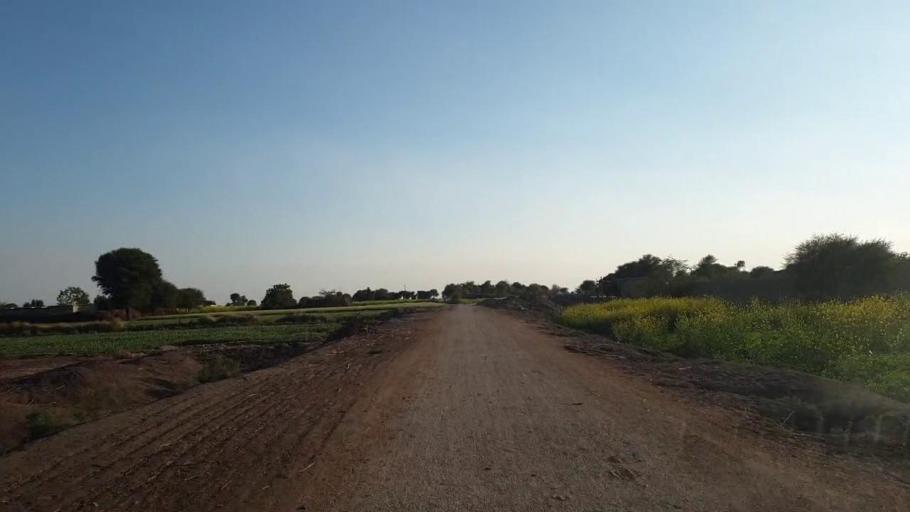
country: PK
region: Sindh
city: Shahpur Chakar
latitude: 26.1484
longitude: 68.5292
